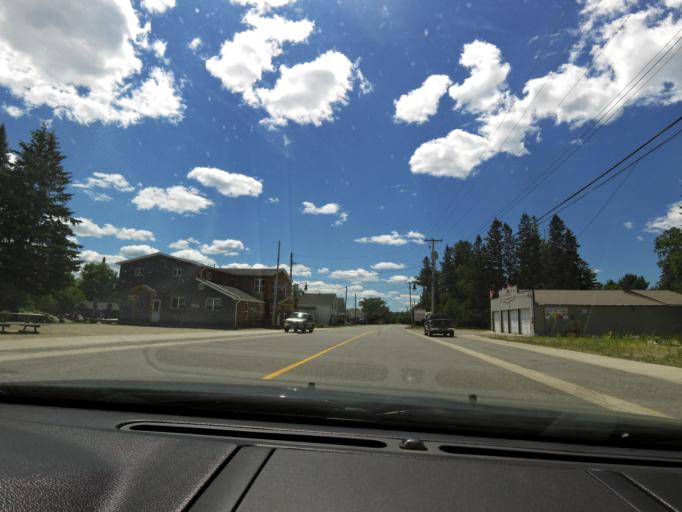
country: CA
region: Ontario
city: Huntsville
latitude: 45.5549
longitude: -79.2242
